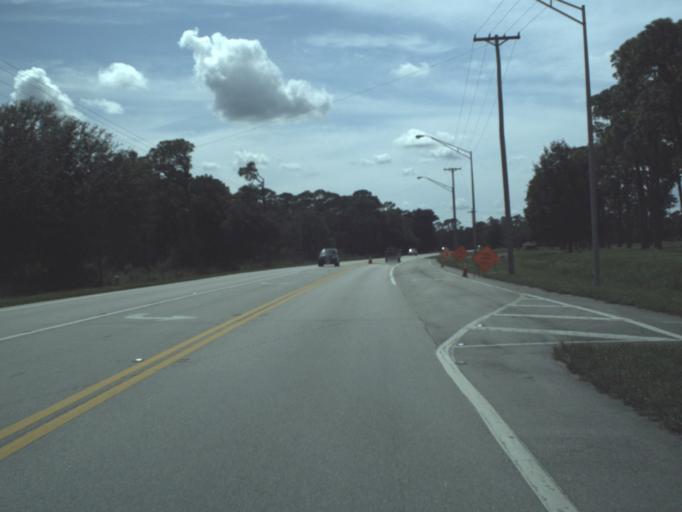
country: US
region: Florida
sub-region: Highlands County
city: Sebring
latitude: 27.4149
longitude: -81.4466
